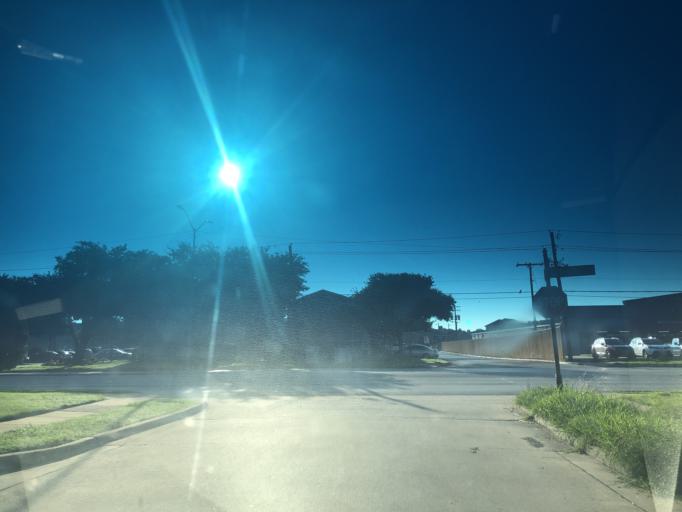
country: US
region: Texas
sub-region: Dallas County
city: Grand Prairie
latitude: 32.6997
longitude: -97.0159
